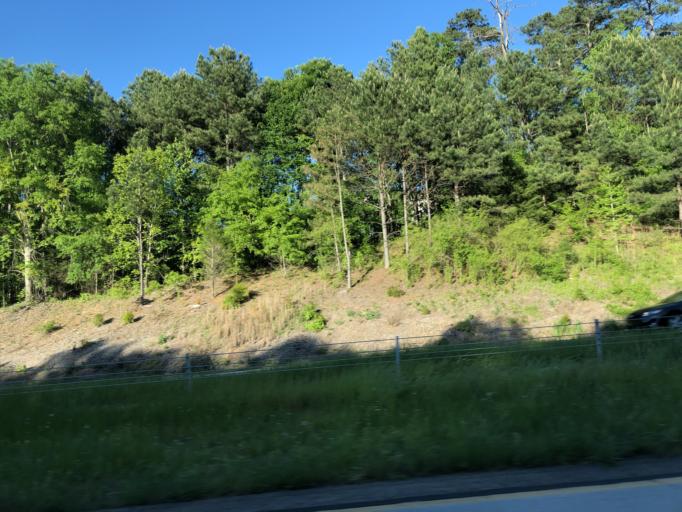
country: US
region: Georgia
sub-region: Oconee County
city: Bogart
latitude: 33.9273
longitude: -83.4670
